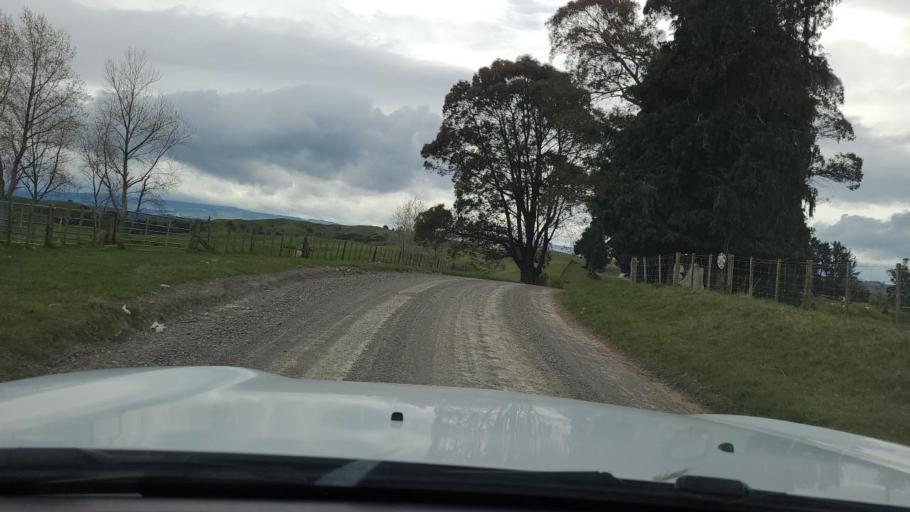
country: NZ
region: Hawke's Bay
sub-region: Napier City
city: Napier
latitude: -39.3172
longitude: 176.8373
